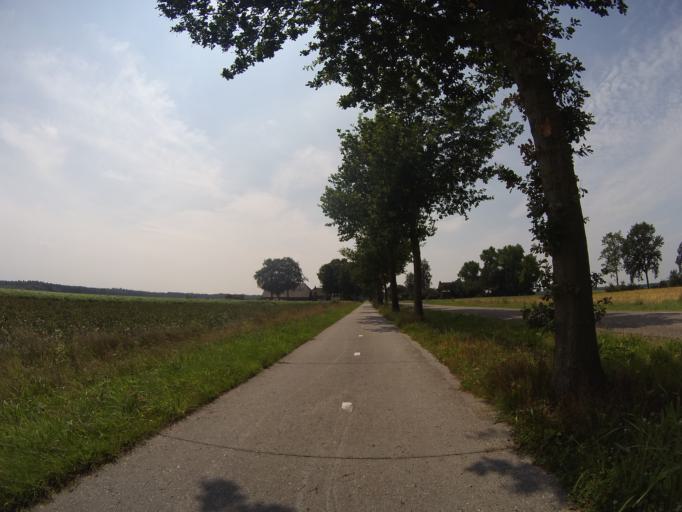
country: NL
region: Drenthe
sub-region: Gemeente Coevorden
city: Sleen
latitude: 52.8352
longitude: 6.7185
